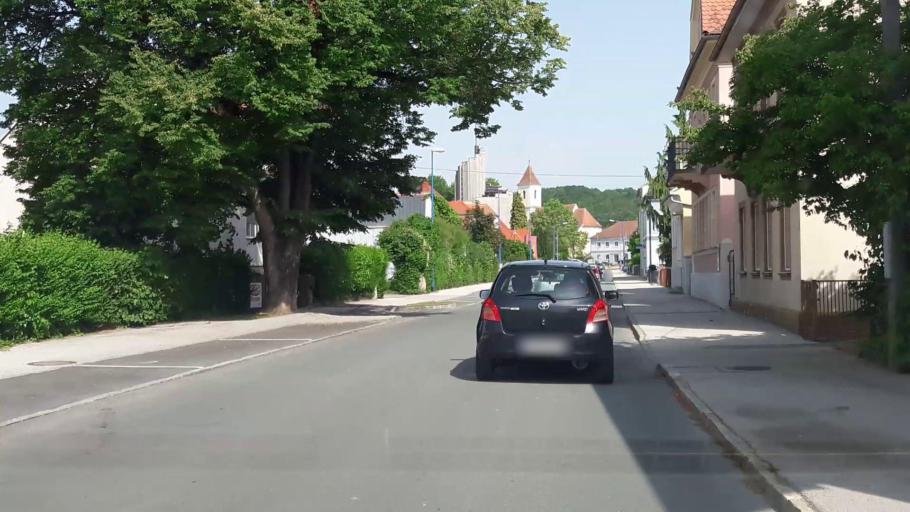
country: AT
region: Burgenland
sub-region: Politischer Bezirk Gussing
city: Stegersbach
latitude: 47.1601
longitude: 16.1614
